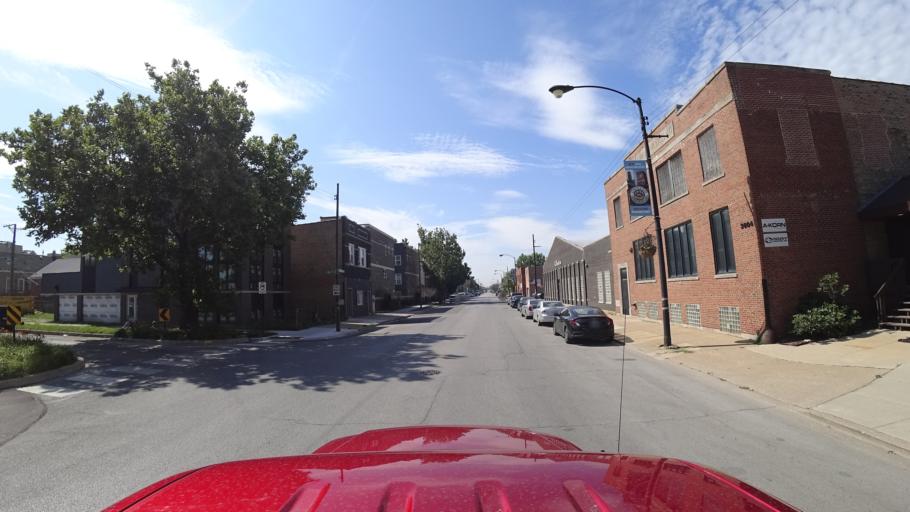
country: US
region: Illinois
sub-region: Cook County
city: Chicago
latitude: 41.8287
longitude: -87.6510
